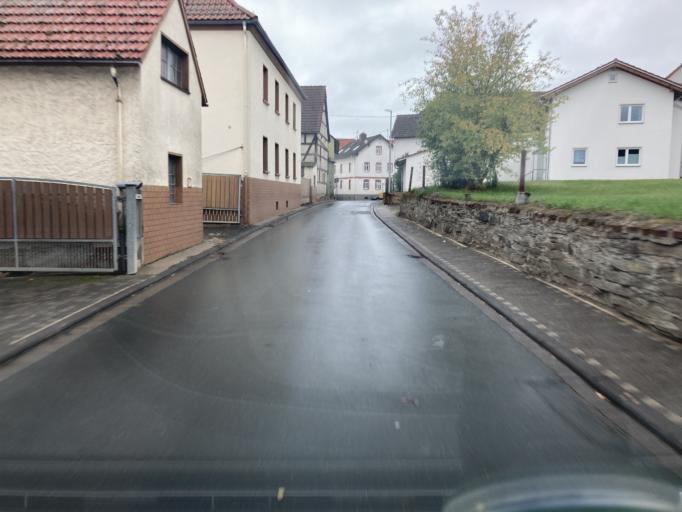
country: DE
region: Hesse
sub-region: Regierungsbezirk Darmstadt
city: Usingen
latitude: 50.3568
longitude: 8.5382
